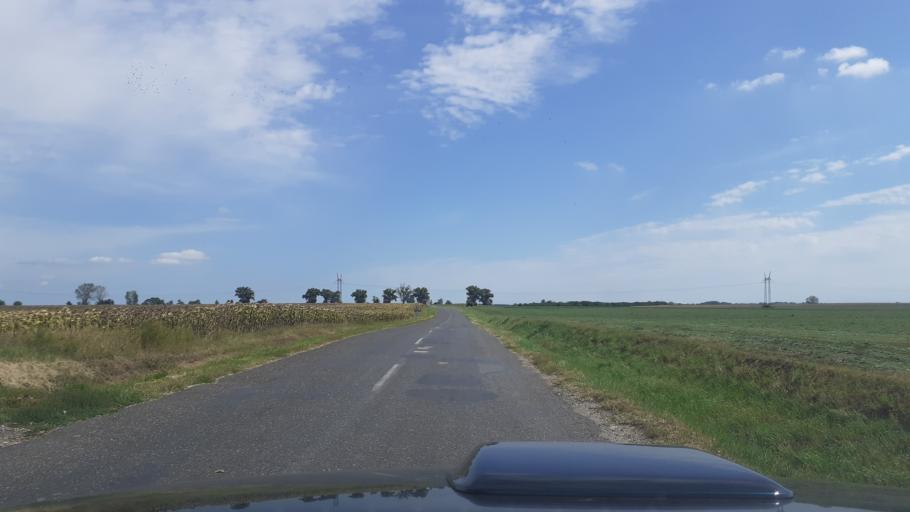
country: HU
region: Fejer
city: Seregelyes
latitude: 47.1492
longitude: 18.5762
